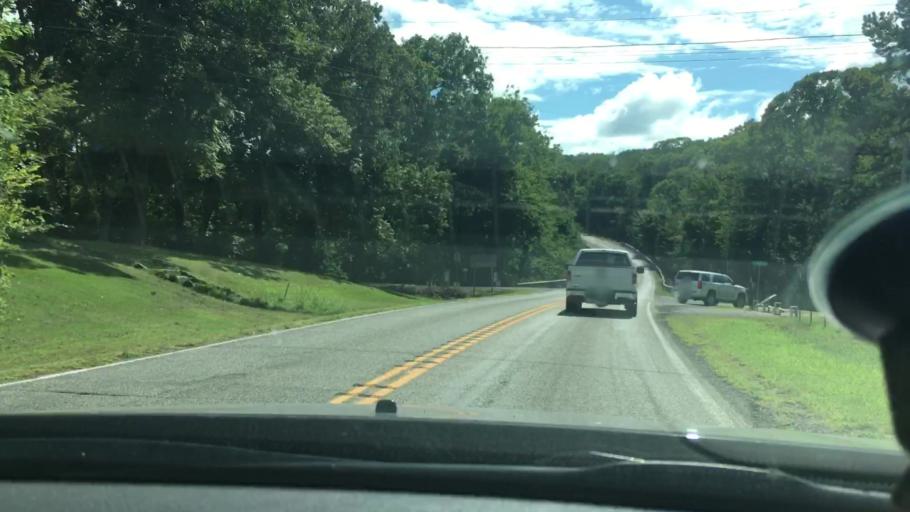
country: US
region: Oklahoma
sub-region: Sequoyah County
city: Vian
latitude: 35.6363
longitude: -94.9615
